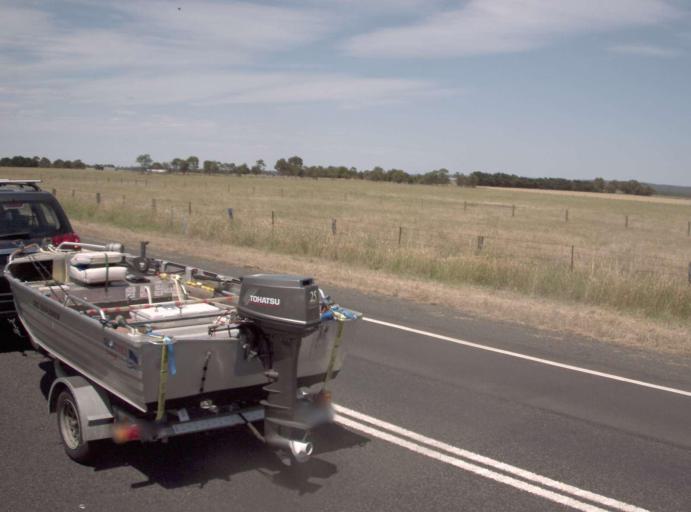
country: AU
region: Victoria
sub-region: Wellington
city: Heyfield
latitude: -38.1269
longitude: 146.8366
